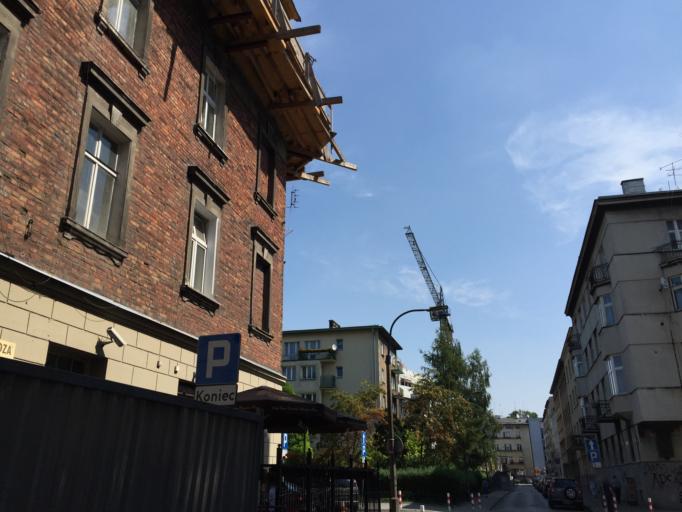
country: PL
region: Lesser Poland Voivodeship
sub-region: Krakow
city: Krakow
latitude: 50.0552
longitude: 19.9219
